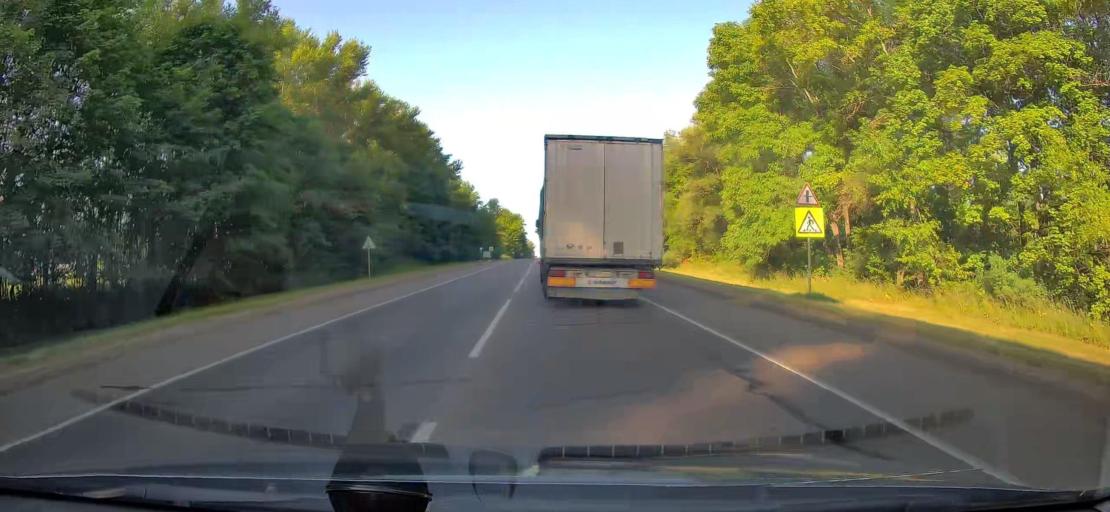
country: RU
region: Tula
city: Chern'
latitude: 53.4634
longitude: 36.9480
